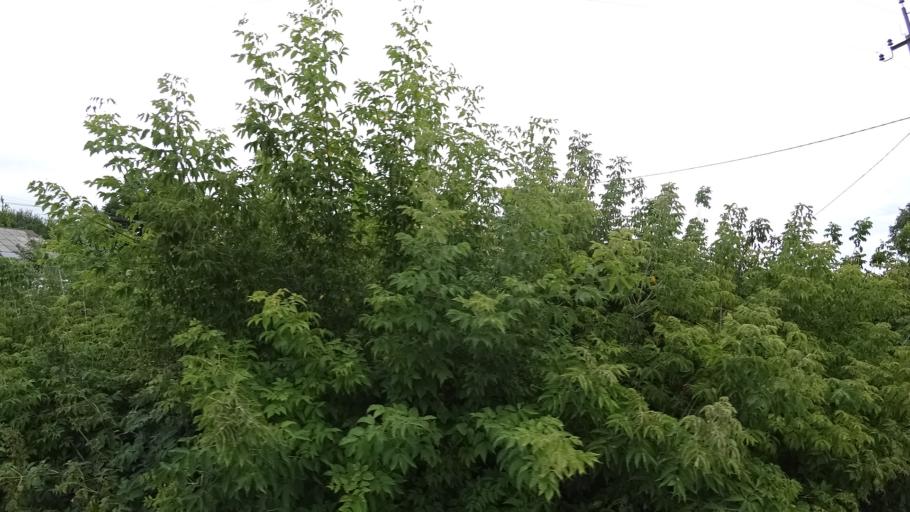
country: RU
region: Primorskiy
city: Chernigovka
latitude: 44.3401
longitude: 132.5760
